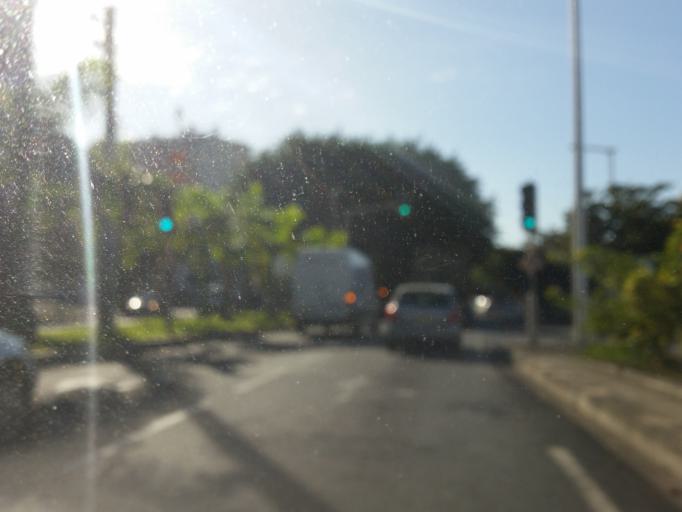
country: RE
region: Reunion
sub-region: Reunion
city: Saint-Denis
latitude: -20.8902
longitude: 55.4603
